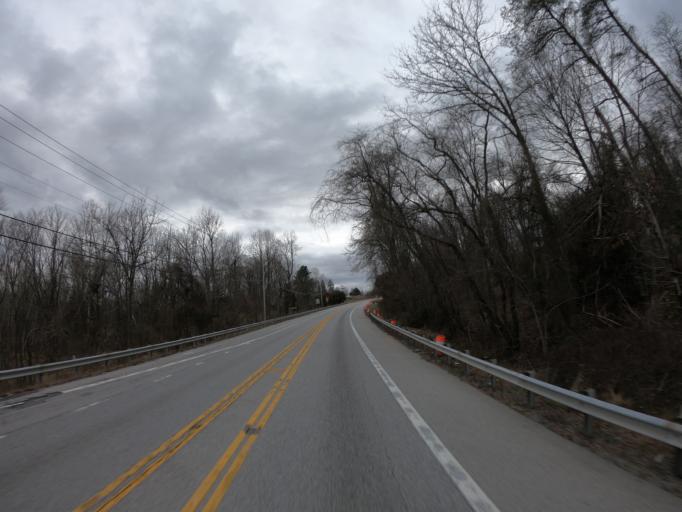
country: US
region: Maryland
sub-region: Carroll County
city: Sykesville
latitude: 39.2841
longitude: -76.9649
